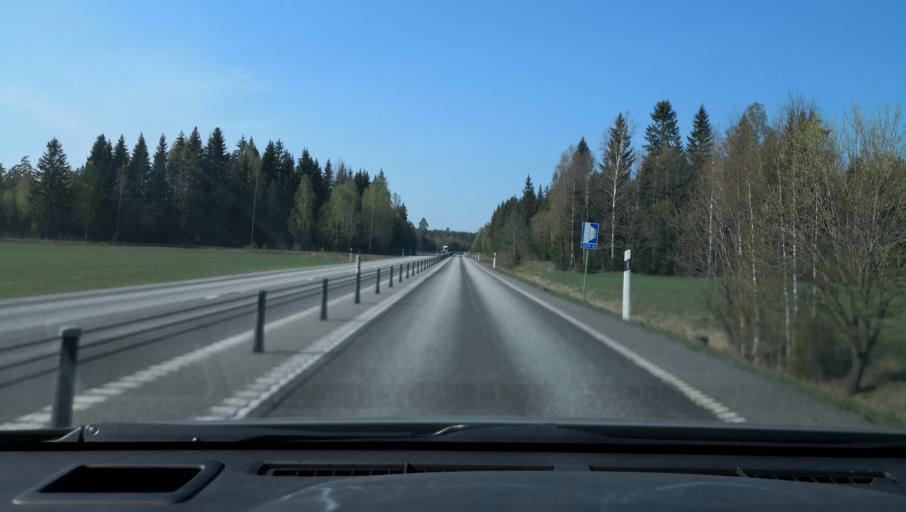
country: SE
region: Uppsala
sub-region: Heby Kommun
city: Tarnsjo
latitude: 60.1750
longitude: 16.9519
